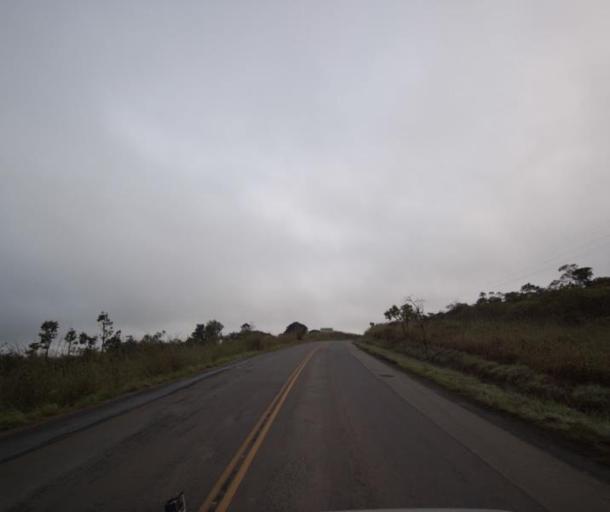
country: BR
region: Goias
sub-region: Pirenopolis
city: Pirenopolis
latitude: -15.8097
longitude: -48.7824
